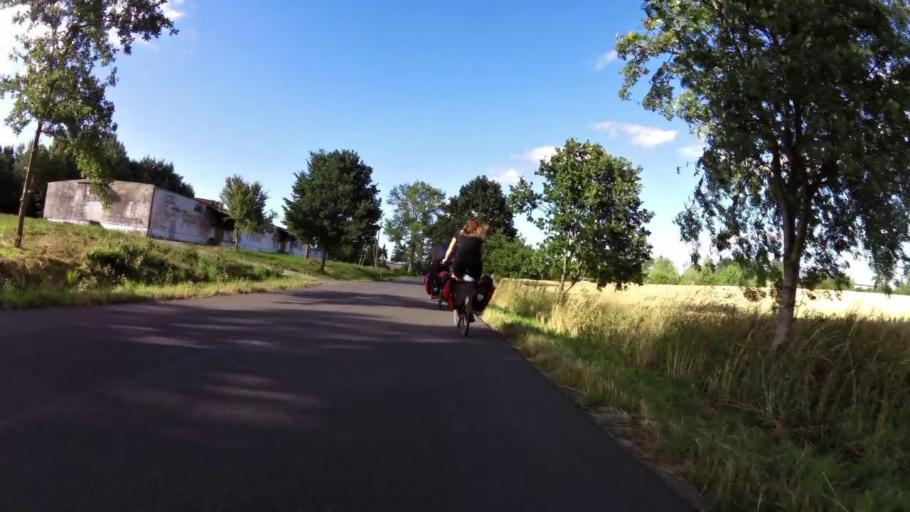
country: PL
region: West Pomeranian Voivodeship
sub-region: Powiat swidwinski
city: Swidwin
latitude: 53.6947
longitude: 15.7821
